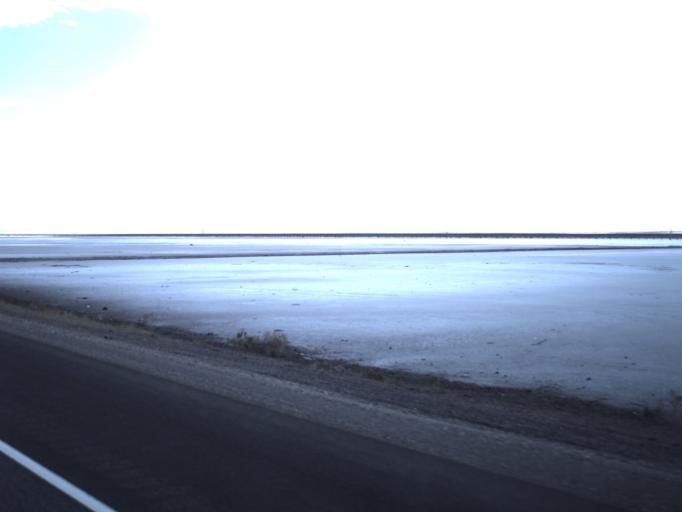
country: US
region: Utah
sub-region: Tooele County
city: Wendover
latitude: 40.7318
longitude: -113.5380
